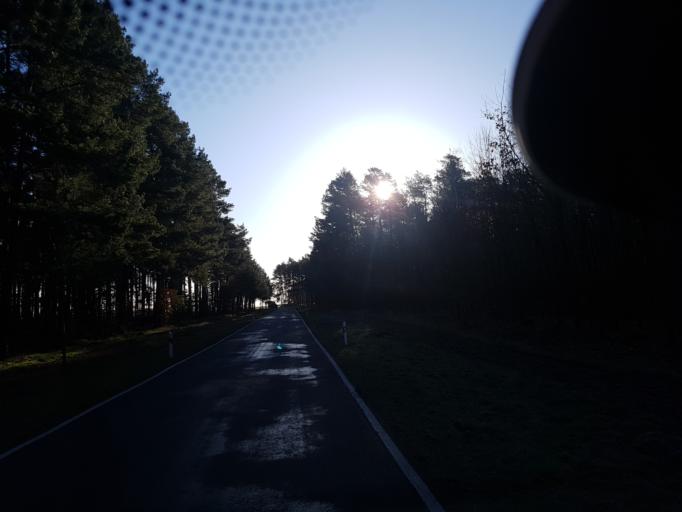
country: DE
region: Brandenburg
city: Jamlitz
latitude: 52.0426
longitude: 14.3976
